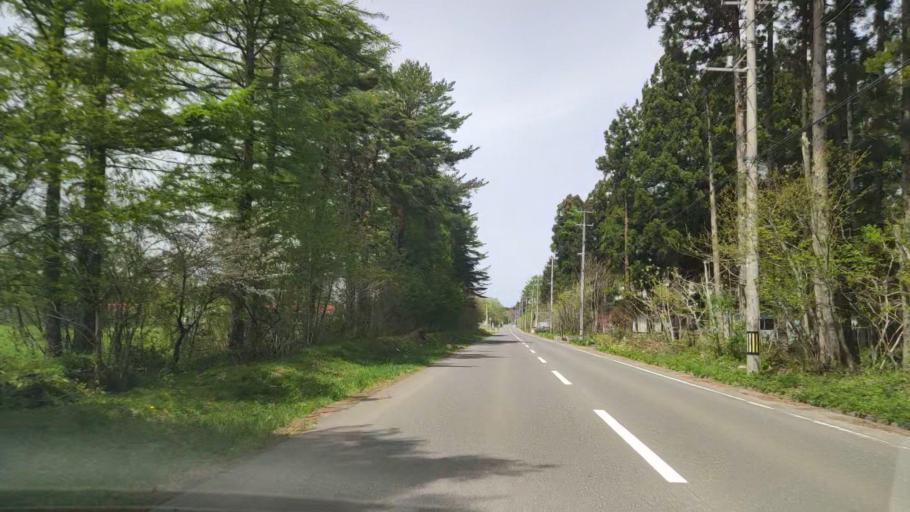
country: JP
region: Aomori
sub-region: Misawa Shi
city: Inuotose
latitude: 40.7159
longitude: 141.1436
